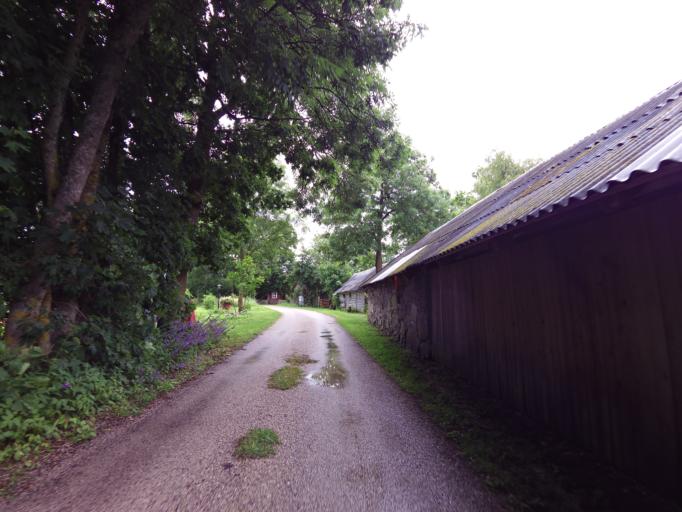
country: EE
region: Laeaene
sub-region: Vormsi vald
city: Hullo
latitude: 59.0173
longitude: 23.3390
